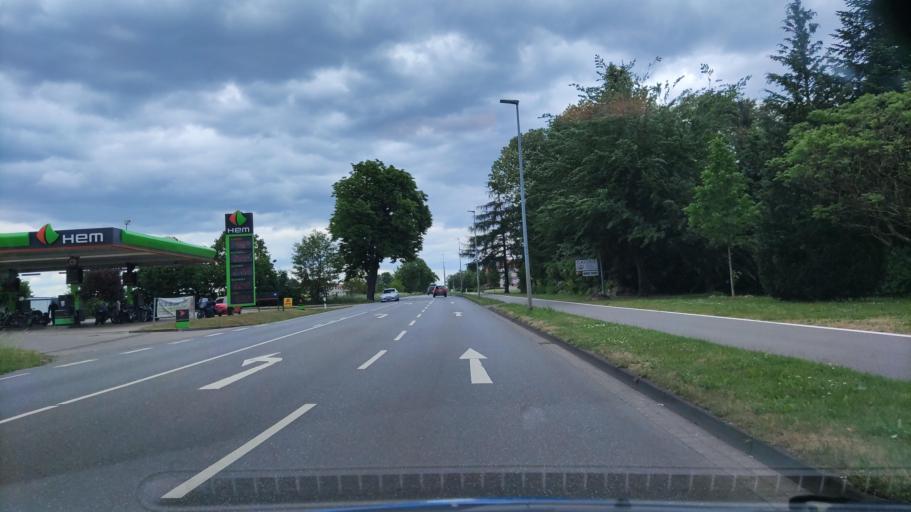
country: DE
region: Mecklenburg-Vorpommern
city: Parchim
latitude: 53.4345
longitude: 11.8702
